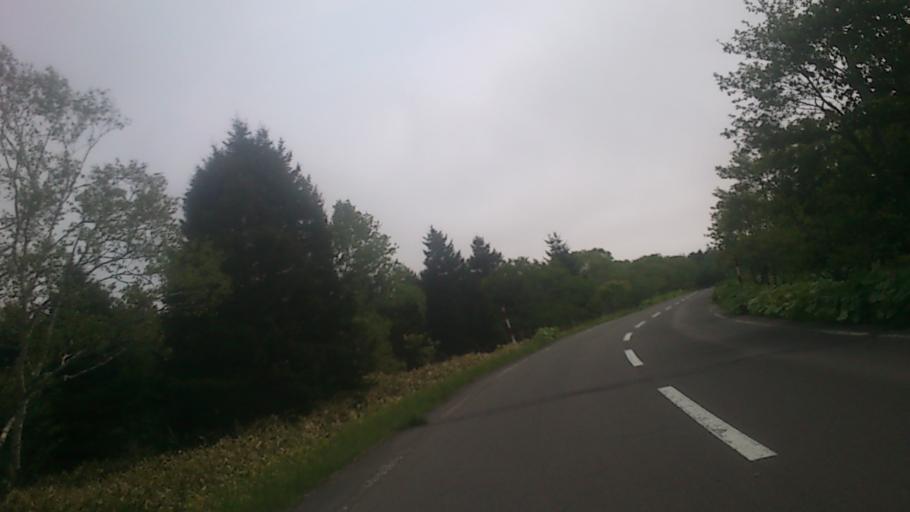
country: JP
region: Hokkaido
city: Nemuro
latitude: 43.1900
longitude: 145.3264
